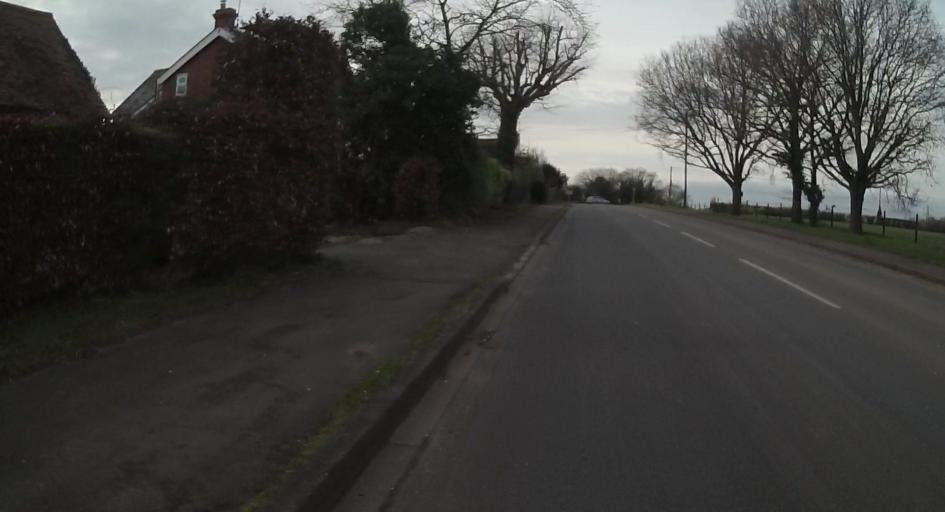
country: GB
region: England
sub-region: West Berkshire
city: Calcot
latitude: 51.4163
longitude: -1.0558
